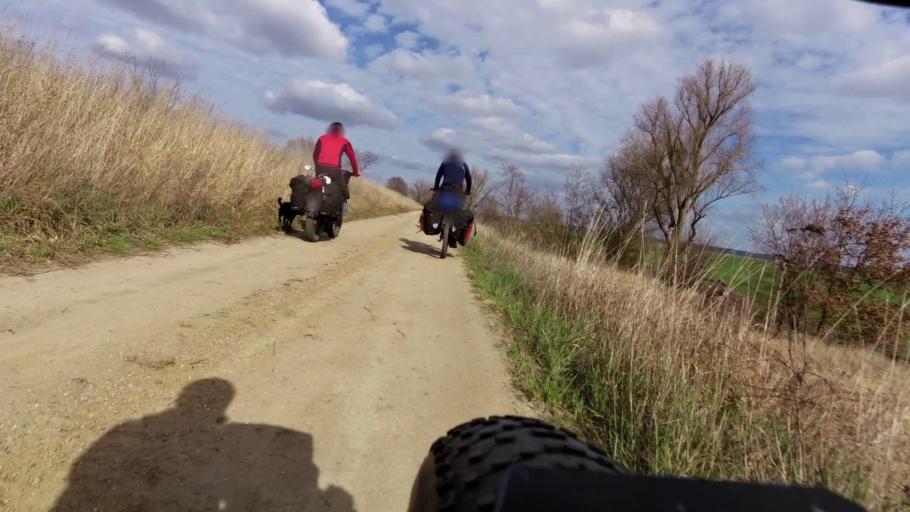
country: DE
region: Brandenburg
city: Lebus
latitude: 52.4369
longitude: 14.5779
